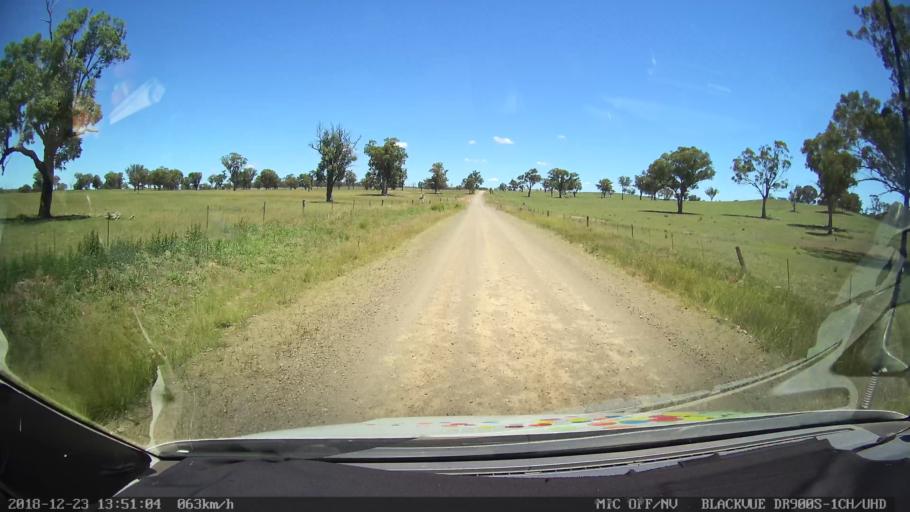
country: AU
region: New South Wales
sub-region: Tamworth Municipality
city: Manilla
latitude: -30.5363
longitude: 151.1057
